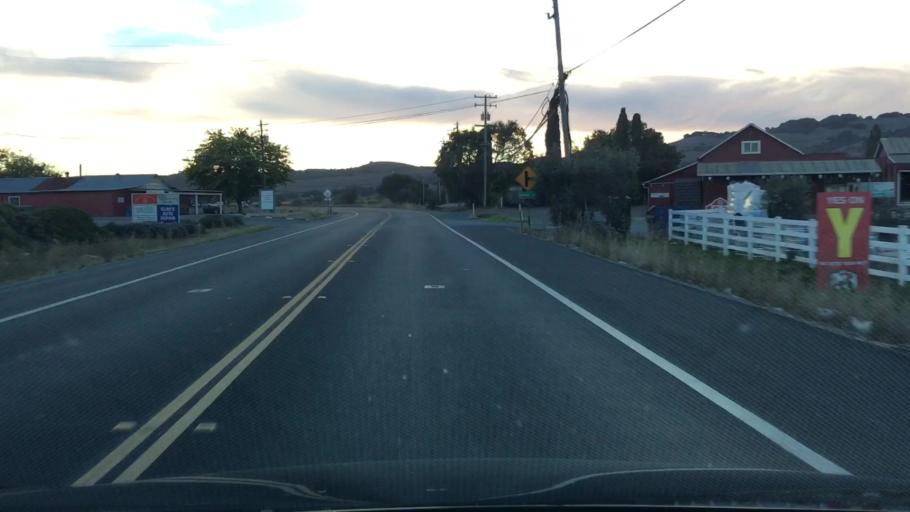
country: US
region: California
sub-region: Sonoma County
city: El Verano
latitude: 38.2886
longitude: -122.4908
